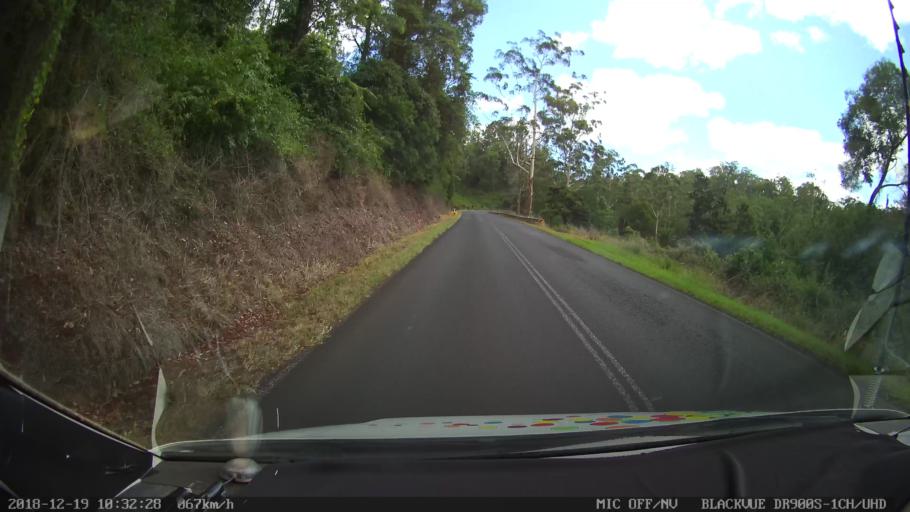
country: AU
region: New South Wales
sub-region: Lismore Municipality
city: Larnook
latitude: -28.5814
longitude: 153.1213
